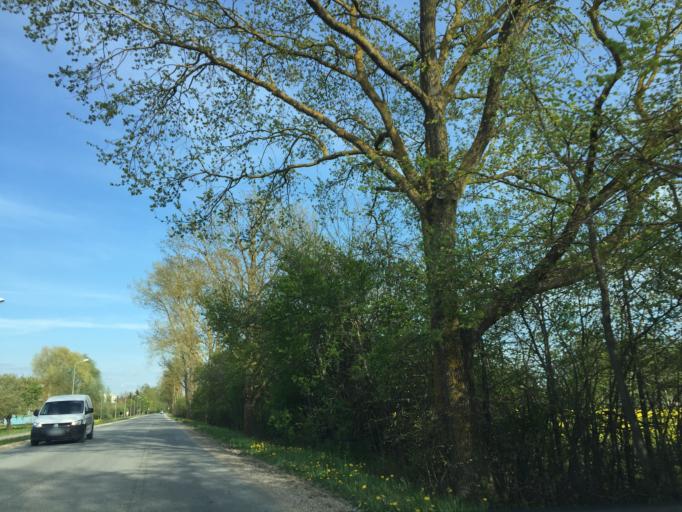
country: LV
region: Bauskas Rajons
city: Bauska
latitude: 56.3987
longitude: 24.1869
